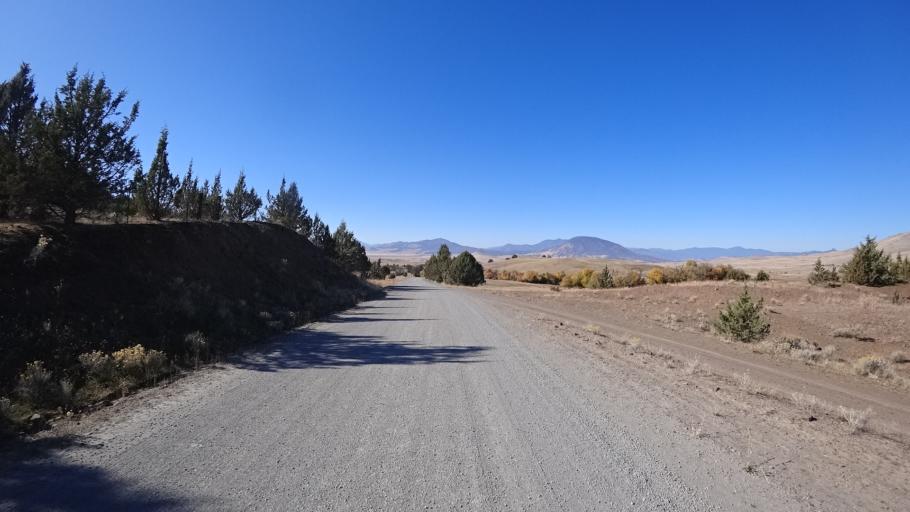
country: US
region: California
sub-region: Siskiyou County
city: Montague
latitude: 41.8080
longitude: -122.3739
